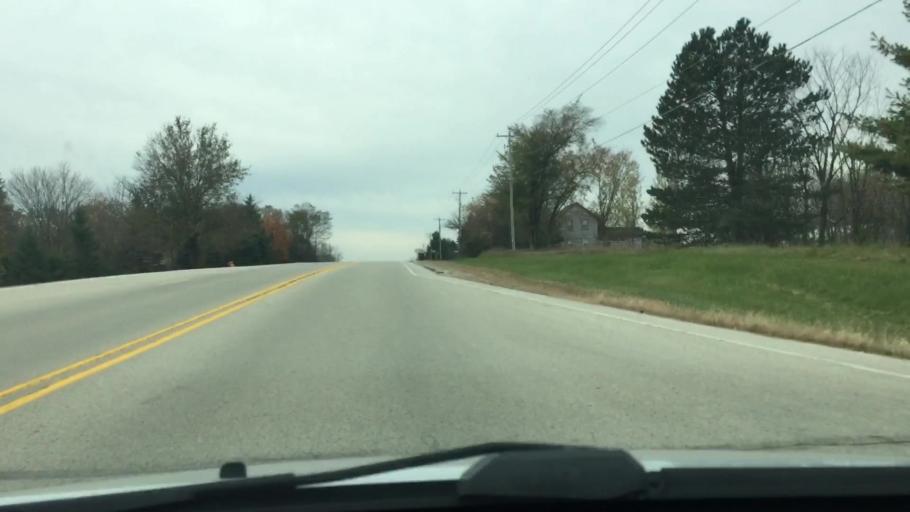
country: US
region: Wisconsin
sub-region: Waukesha County
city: Mukwonago
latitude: 42.8875
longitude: -88.2837
